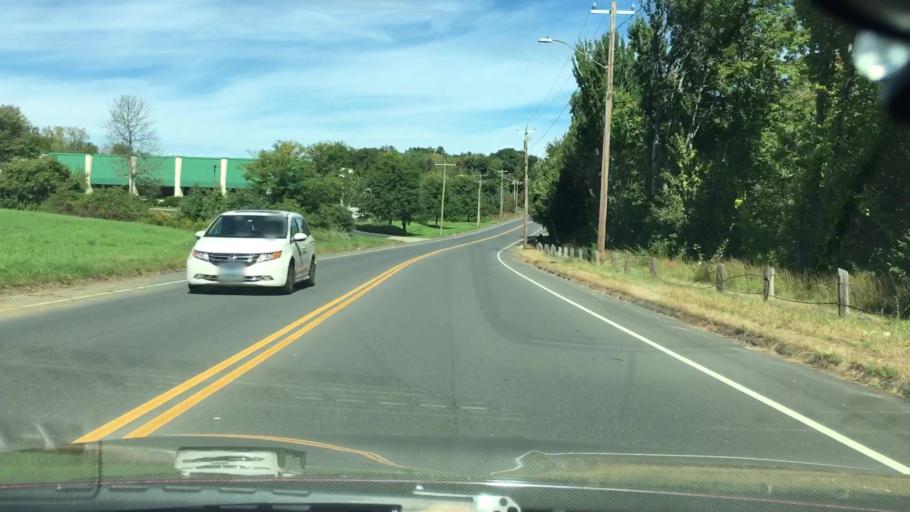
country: US
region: Connecticut
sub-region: Litchfield County
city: Terryville
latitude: 41.6885
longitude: -72.9844
